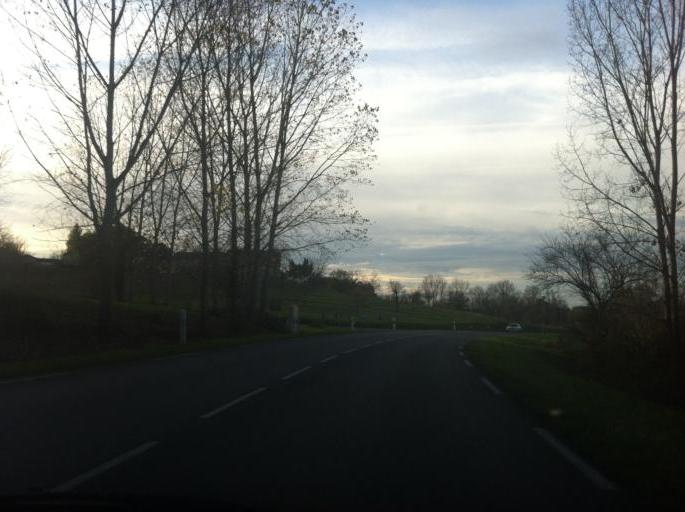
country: FR
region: Aquitaine
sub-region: Departement de la Dordogne
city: Tocane-Saint-Apre
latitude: 45.2576
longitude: 0.5112
